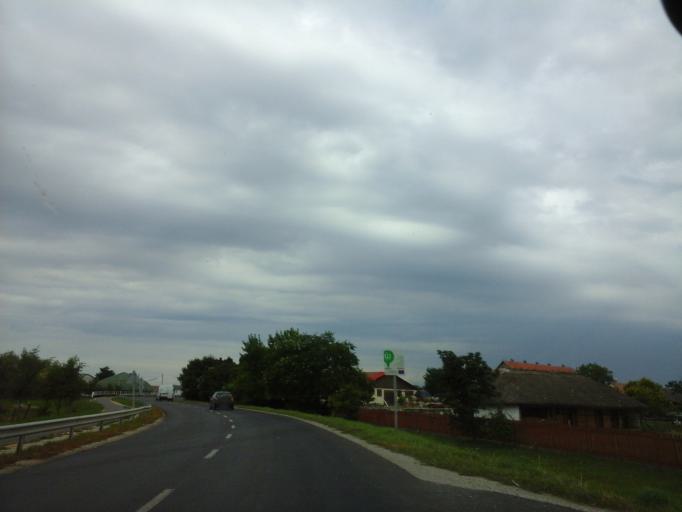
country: HU
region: Hajdu-Bihar
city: Balmazujvaros
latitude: 47.5994
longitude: 21.3374
